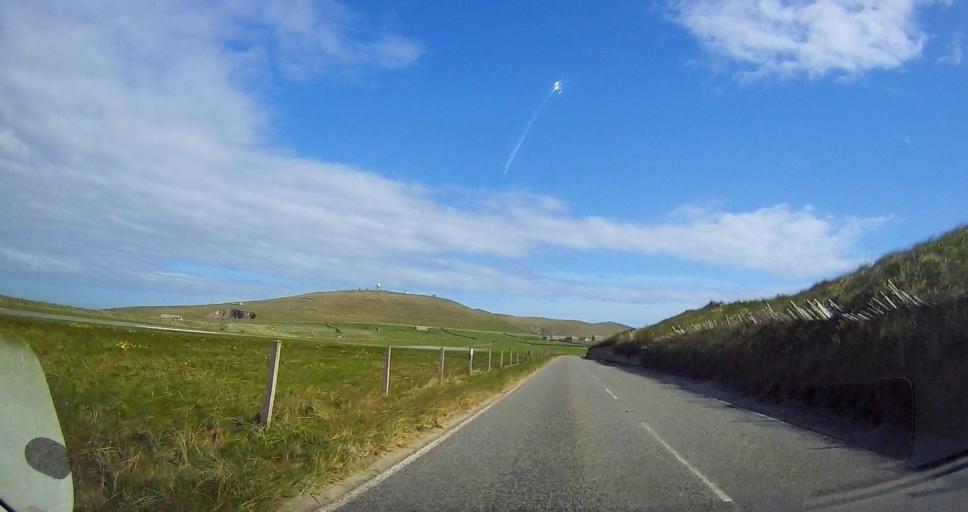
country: GB
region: Scotland
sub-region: Shetland Islands
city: Sandwick
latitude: 59.8746
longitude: -1.2910
